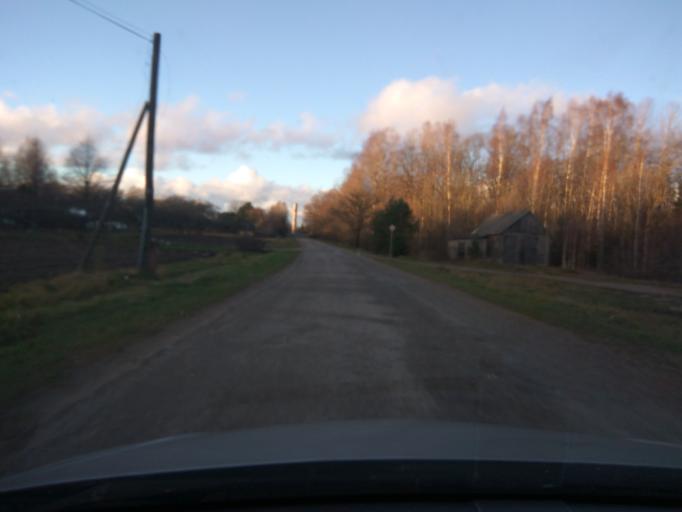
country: LV
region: Aizpute
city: Aizpute
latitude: 56.8298
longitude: 21.7742
